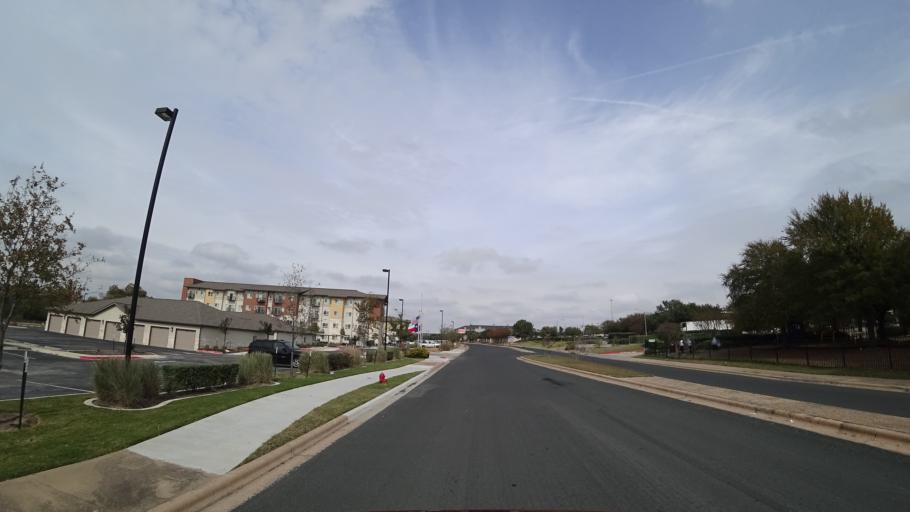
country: US
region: Texas
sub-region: Travis County
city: Wells Branch
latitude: 30.4350
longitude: -97.6712
